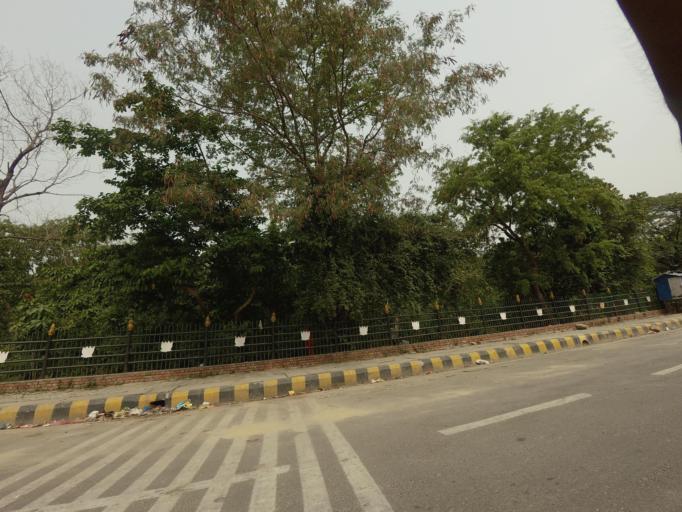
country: IN
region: Uttar Pradesh
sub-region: Maharajganj
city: Nautanwa
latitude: 27.4691
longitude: 83.2838
